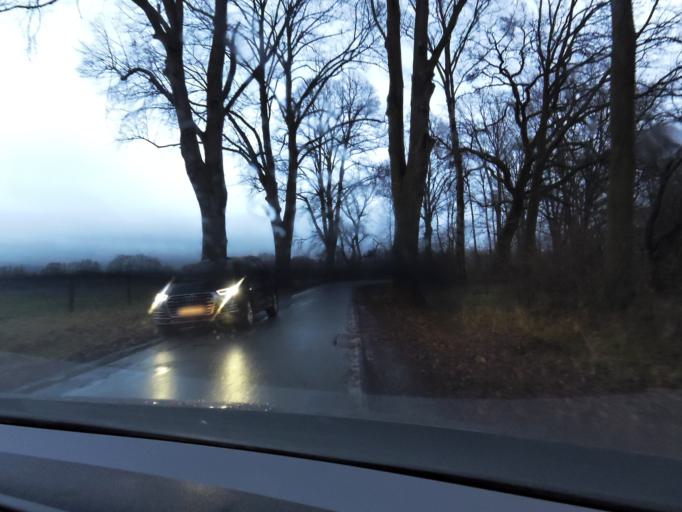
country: DE
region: Schleswig-Holstein
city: Kittlitz
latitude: 53.6600
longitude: 10.8982
